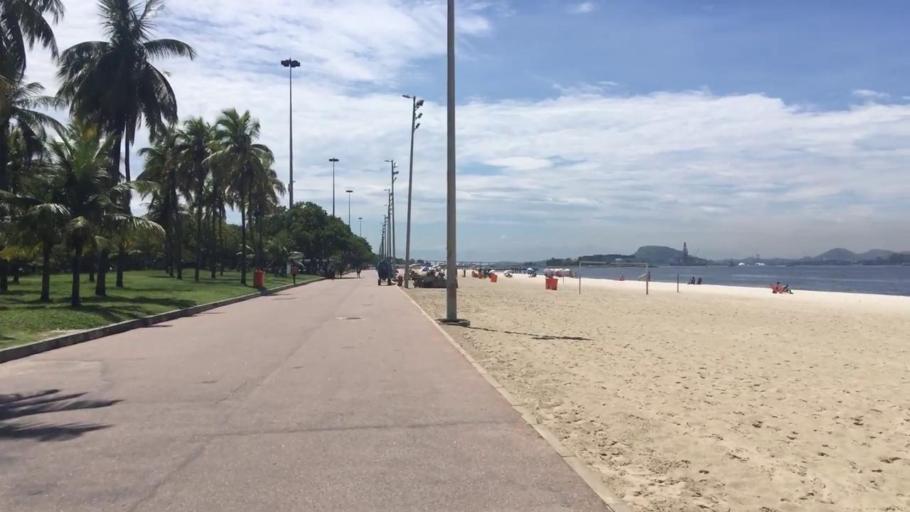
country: BR
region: Rio de Janeiro
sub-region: Rio De Janeiro
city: Rio de Janeiro
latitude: -22.9278
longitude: -43.1709
